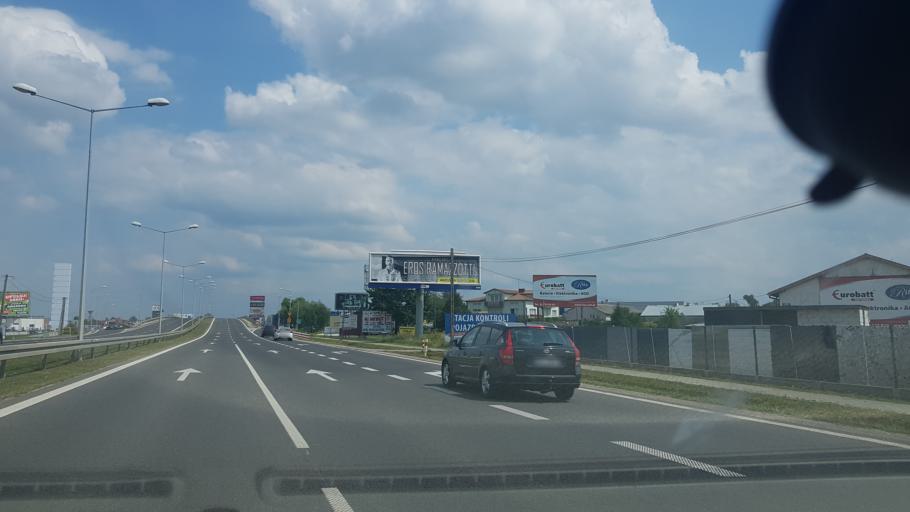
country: PL
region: Masovian Voivodeship
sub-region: Powiat pruszkowski
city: Nowe Grocholice
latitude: 52.1315
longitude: 20.8891
